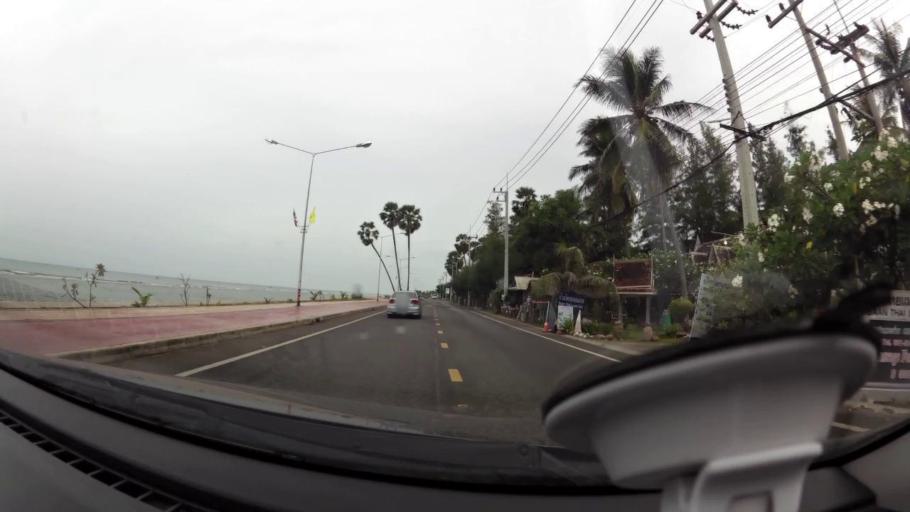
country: TH
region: Prachuap Khiri Khan
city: Pran Buri
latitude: 12.3830
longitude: 99.9995
